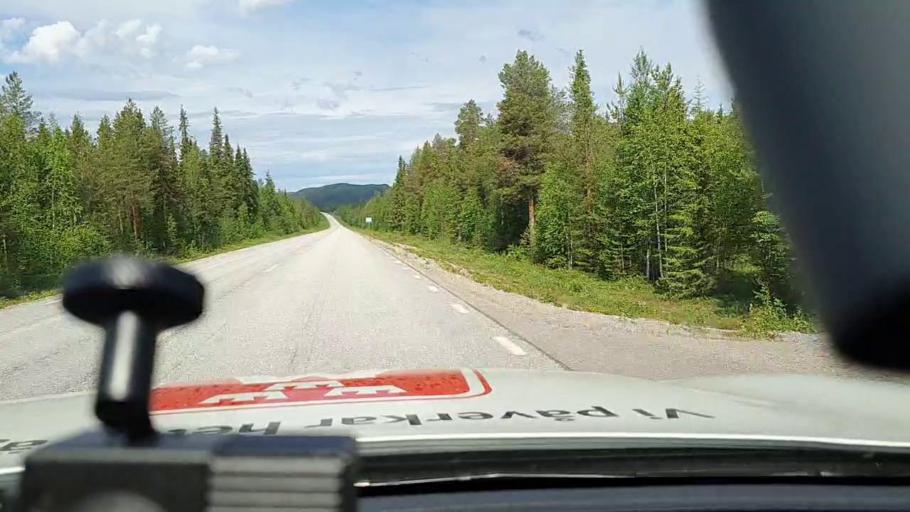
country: SE
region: Norrbotten
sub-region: Jokkmokks Kommun
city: Jokkmokk
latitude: 66.5453
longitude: 20.1351
